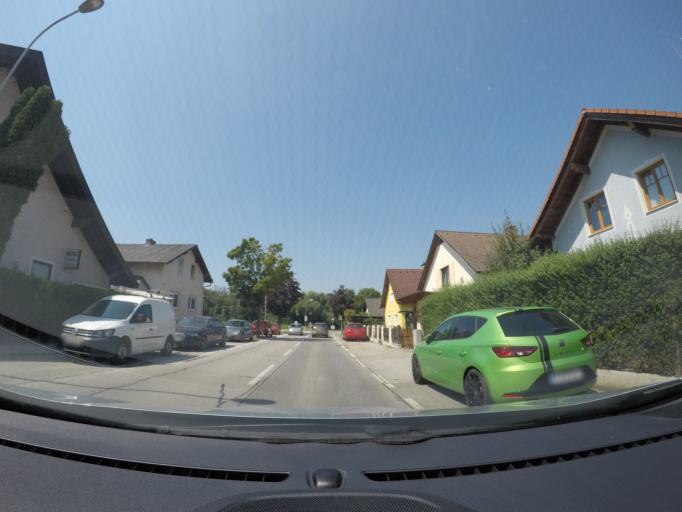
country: AT
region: Lower Austria
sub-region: Politischer Bezirk Sankt Polten
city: Maria-Anzbach
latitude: 48.1908
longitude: 15.9274
